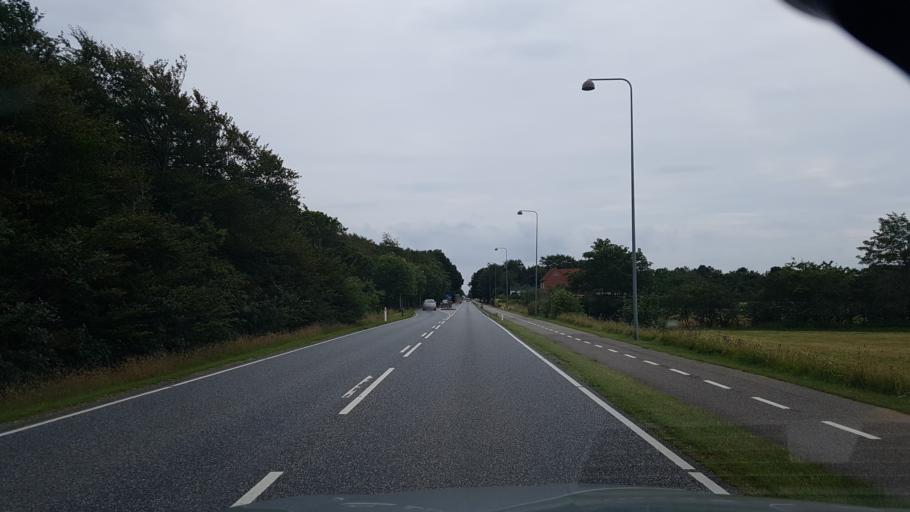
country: DK
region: South Denmark
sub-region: Esbjerg Kommune
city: Ribe
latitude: 55.2815
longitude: 8.7322
